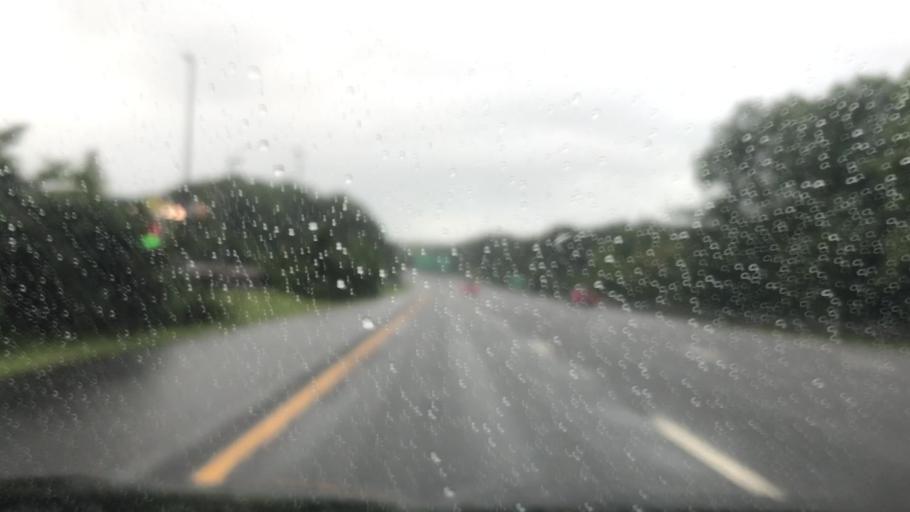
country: US
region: New Jersey
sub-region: Monmouth County
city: Shark River Hills
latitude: 40.1997
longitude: -74.0982
